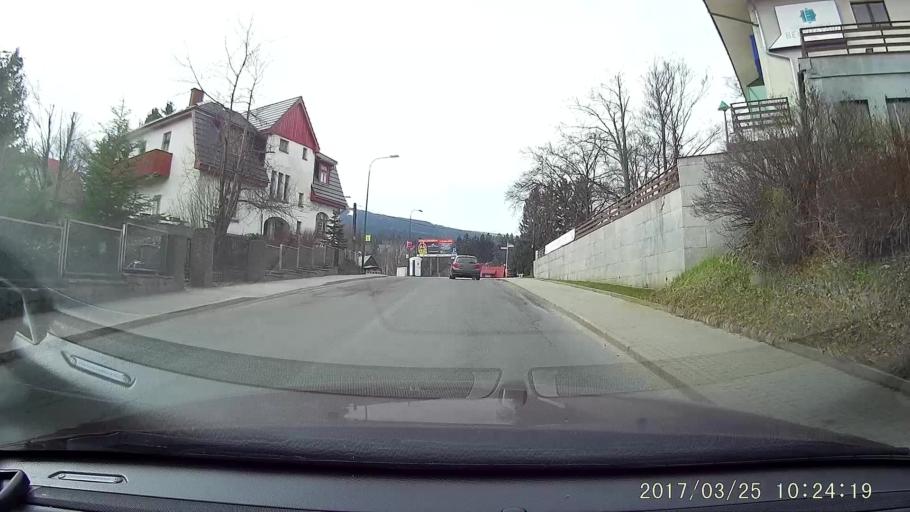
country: PL
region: Lower Silesian Voivodeship
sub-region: Powiat jeleniogorski
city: Szklarska Poreba
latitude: 50.8229
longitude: 15.5272
